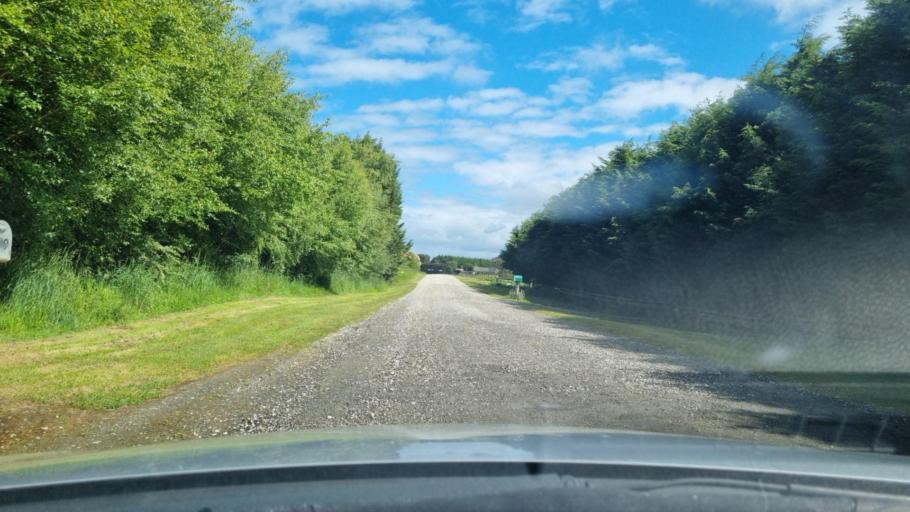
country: NZ
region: Southland
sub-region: Invercargill City
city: Invercargill
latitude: -46.4227
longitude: 168.2937
